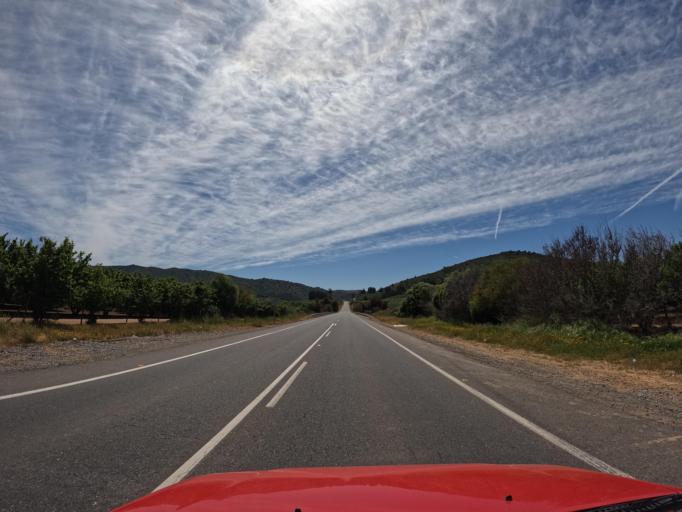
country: CL
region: Maule
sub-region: Provincia de Talca
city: Talca
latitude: -35.2645
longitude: -71.5415
